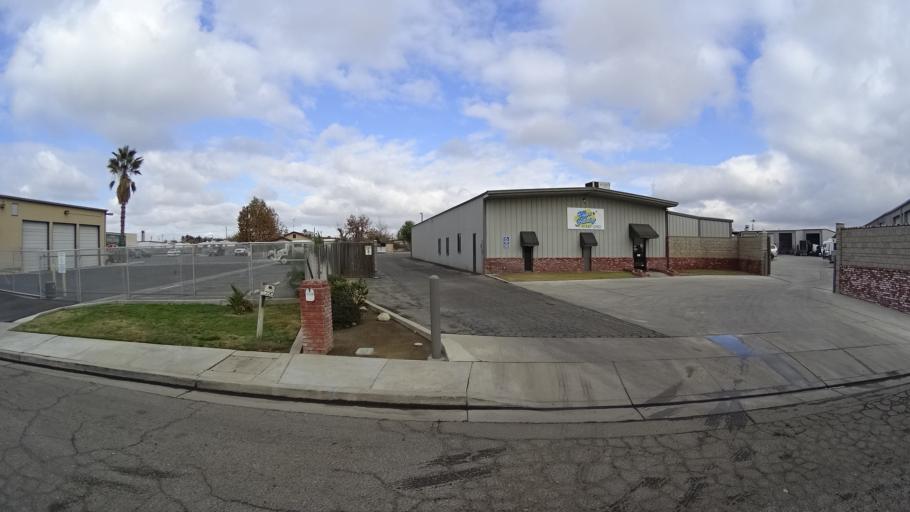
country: US
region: California
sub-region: Kern County
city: Bakersfield
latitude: 35.3332
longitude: -118.9998
